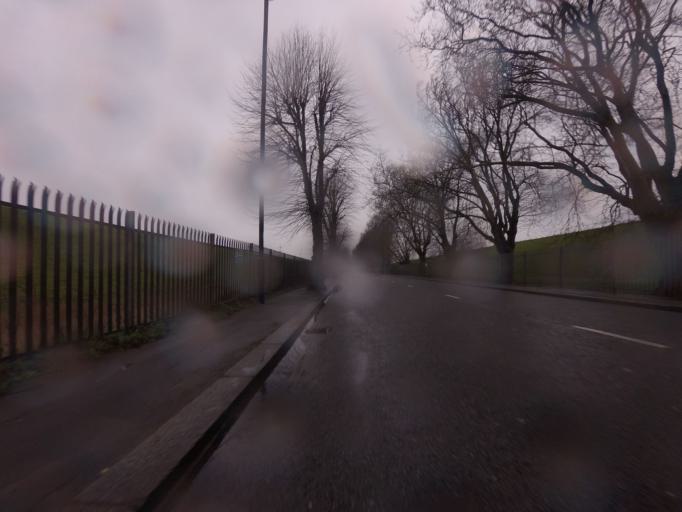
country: GB
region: England
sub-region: Greater London
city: Walthamstow
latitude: 51.6389
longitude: -0.0215
